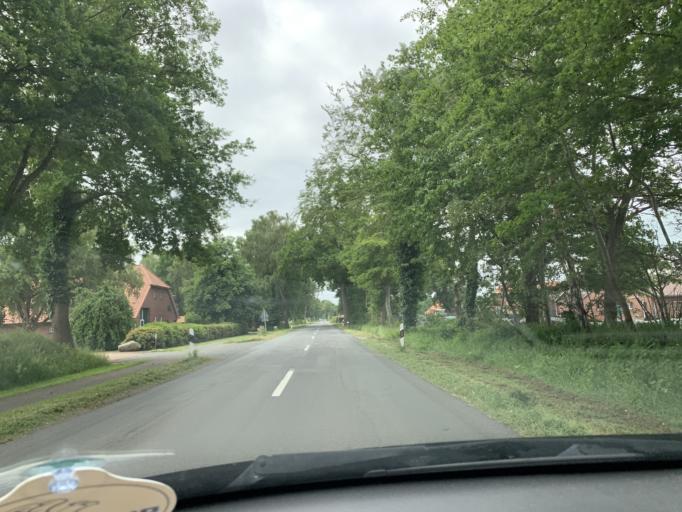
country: DE
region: Lower Saxony
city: Bockhorn
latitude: 53.3417
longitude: 8.0391
